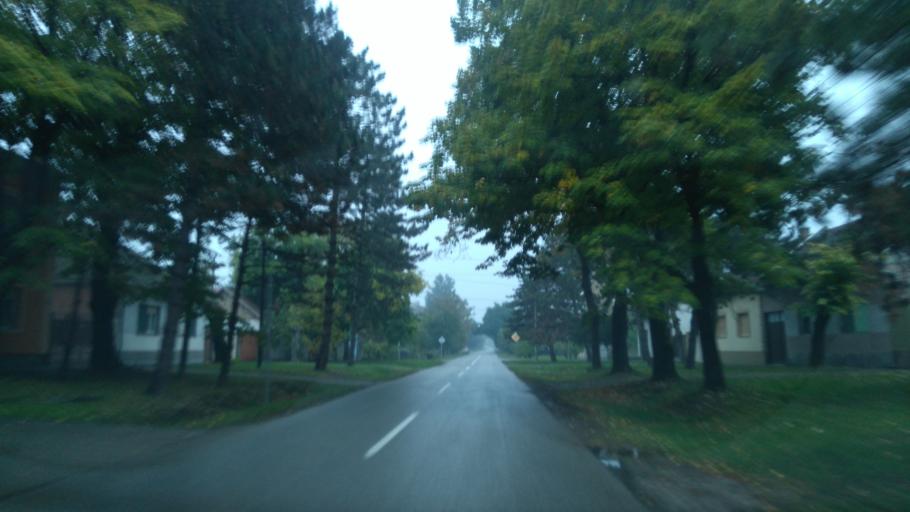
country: RS
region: Autonomna Pokrajina Vojvodina
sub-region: Juznobacki Okrug
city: Becej
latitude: 45.6067
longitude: 20.0419
